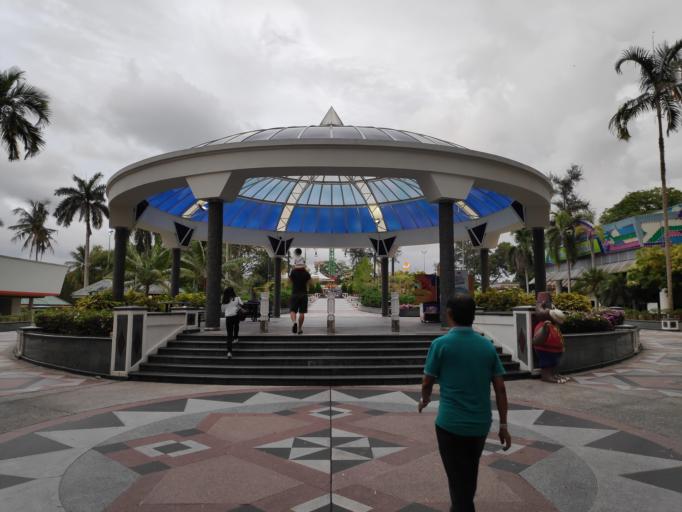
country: BN
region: Brunei and Muara
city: Bandar Seri Begawan
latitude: 4.9375
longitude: 114.8366
